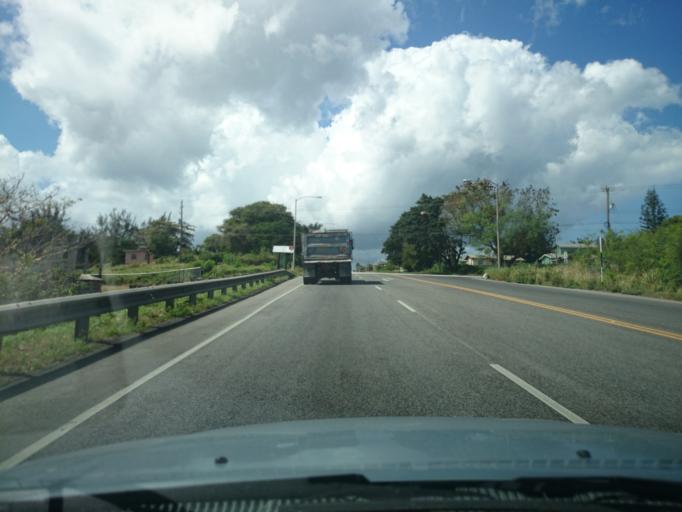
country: BB
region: Saint Michael
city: Bridgetown
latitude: 13.1404
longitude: -59.6142
